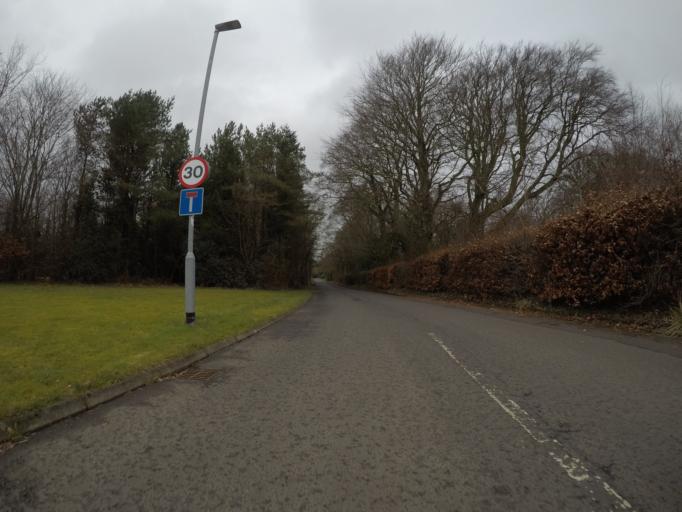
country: GB
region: Scotland
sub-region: North Ayrshire
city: Springside
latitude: 55.6272
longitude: -4.6153
